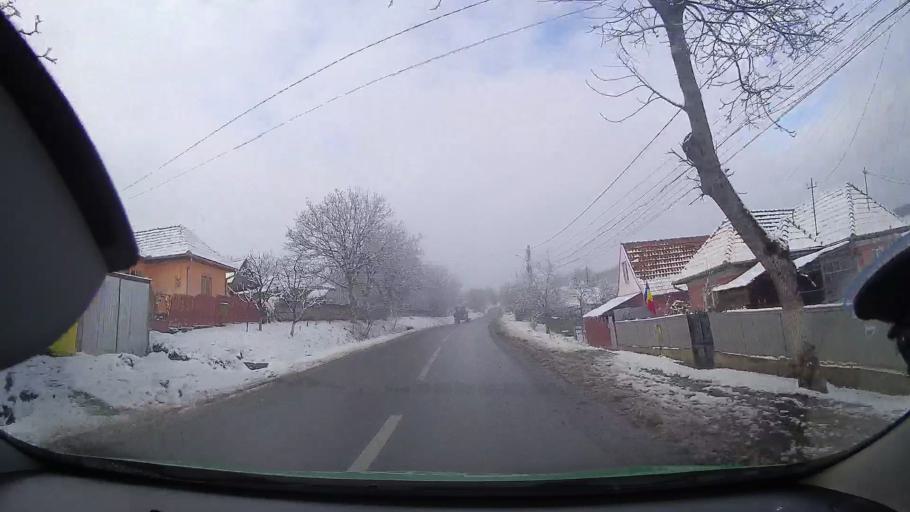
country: RO
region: Mures
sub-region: Comuna Atintis
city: Atintis
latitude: 46.4334
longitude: 24.0993
